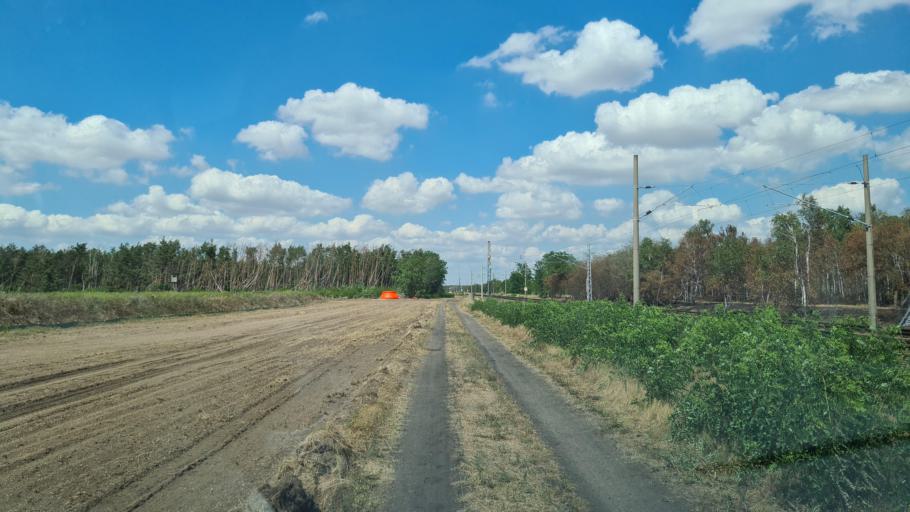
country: DE
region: Brandenburg
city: Muhlberg
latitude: 51.4339
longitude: 13.3042
